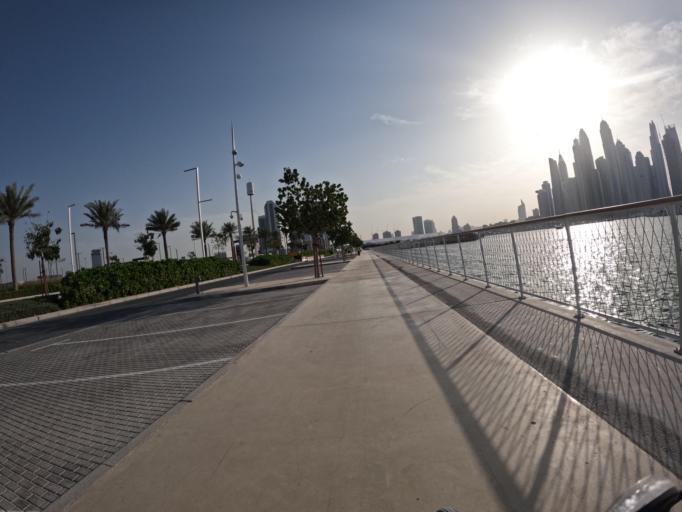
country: AE
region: Dubai
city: Dubai
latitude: 25.0934
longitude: 55.1338
